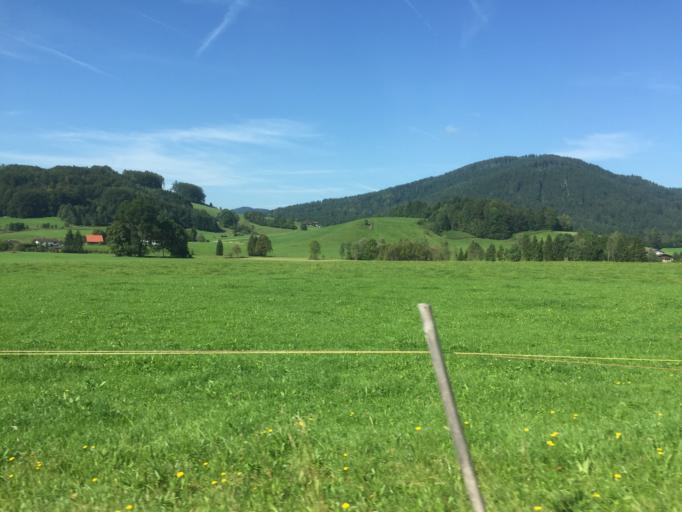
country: DE
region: Bavaria
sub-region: Upper Bavaria
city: Inzell
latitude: 47.7602
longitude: 12.7361
